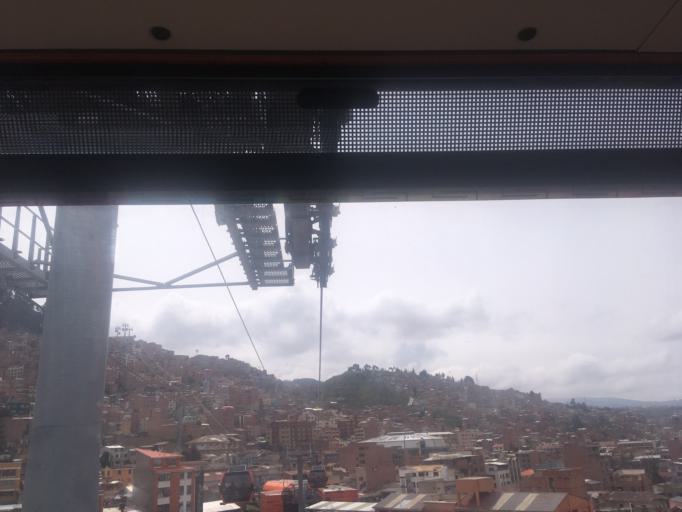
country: BO
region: La Paz
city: La Paz
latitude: -16.4907
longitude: -68.1384
